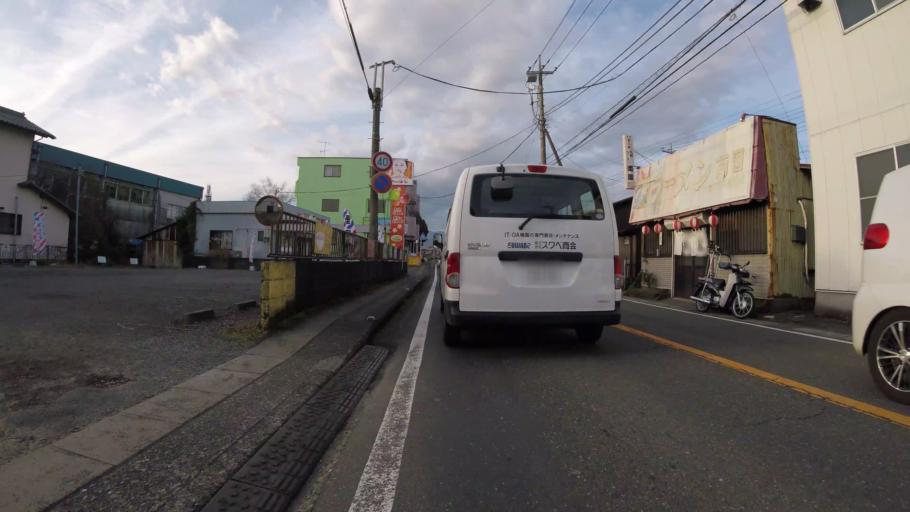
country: JP
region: Shizuoka
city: Mishima
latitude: 35.1093
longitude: 138.9279
